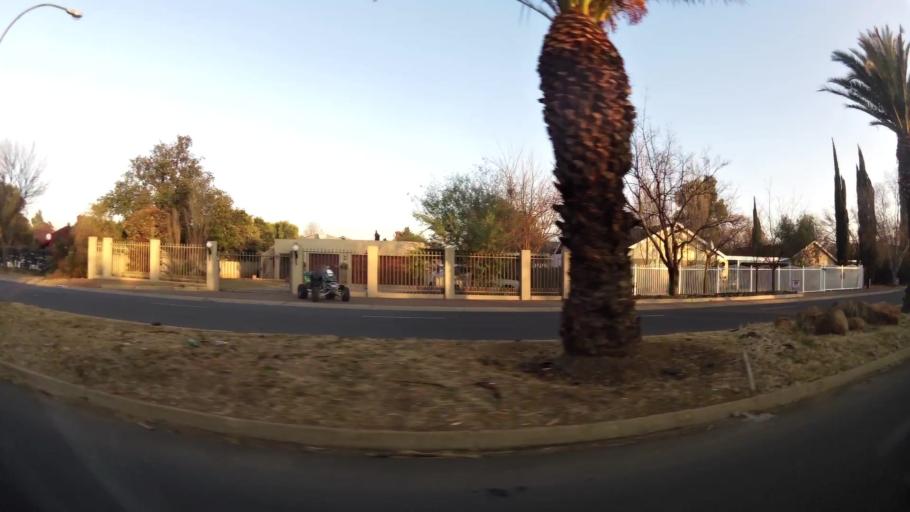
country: ZA
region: Orange Free State
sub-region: Mangaung Metropolitan Municipality
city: Bloemfontein
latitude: -29.1065
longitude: 26.1557
